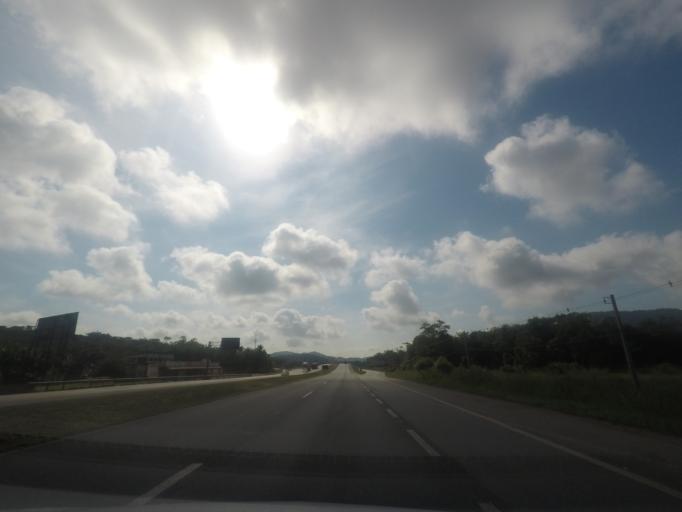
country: BR
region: Parana
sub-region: Antonina
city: Antonina
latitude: -25.5501
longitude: -48.7953
